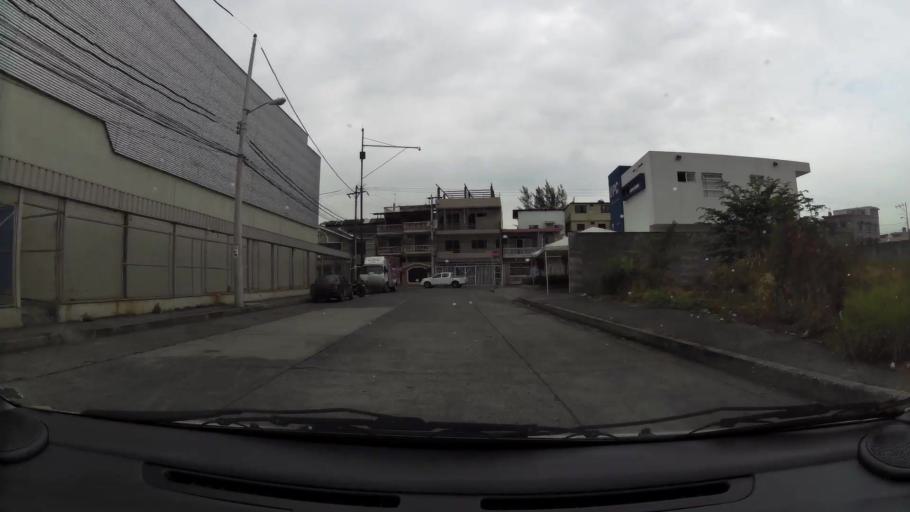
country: EC
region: Guayas
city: Eloy Alfaro
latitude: -2.1428
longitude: -79.8873
